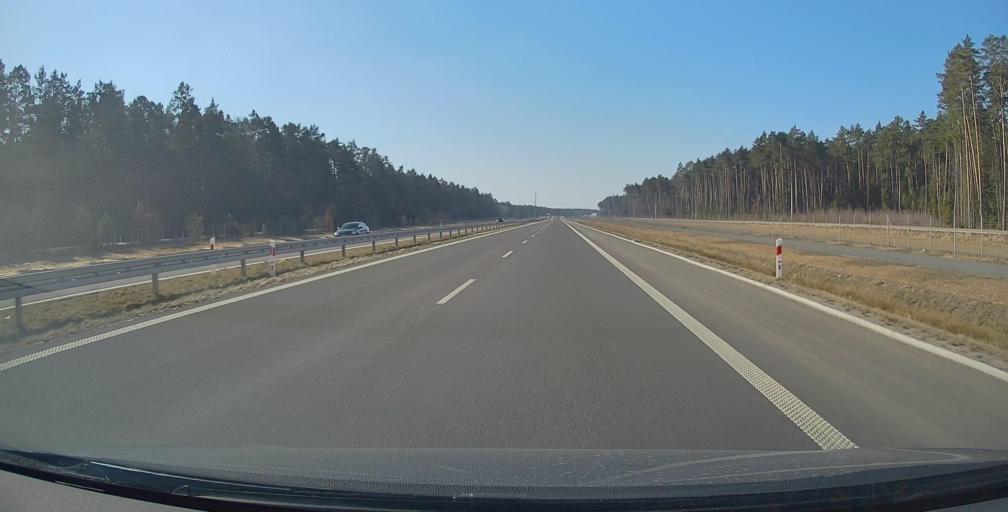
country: PL
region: Lublin Voivodeship
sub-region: Powiat janowski
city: Modliborzyce
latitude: 50.6664
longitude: 22.3218
